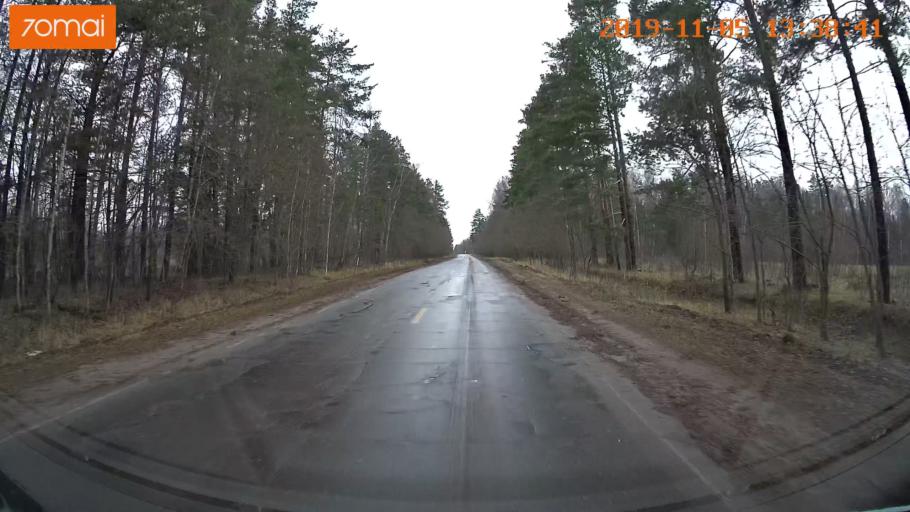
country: RU
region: Ivanovo
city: Shuya
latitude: 56.9338
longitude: 41.3868
